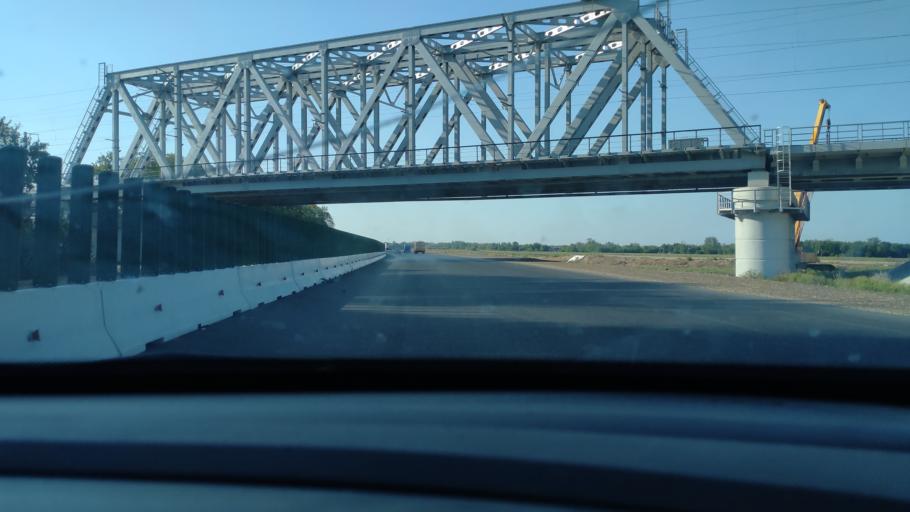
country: RU
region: Krasnodarskiy
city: Medvedovskaya
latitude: 45.4930
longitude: 38.9550
